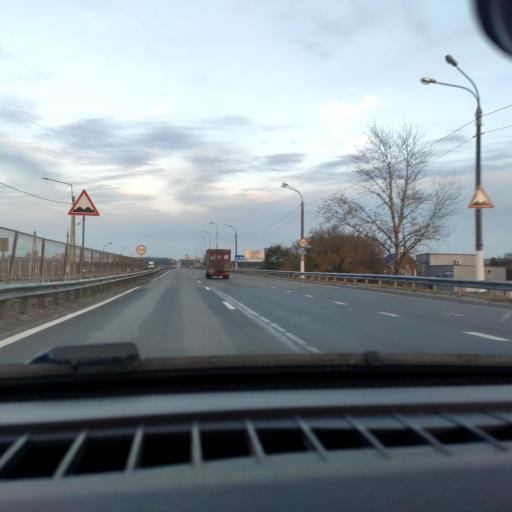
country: RU
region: Voronezj
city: Pridonskoy
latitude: 51.6510
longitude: 39.0637
